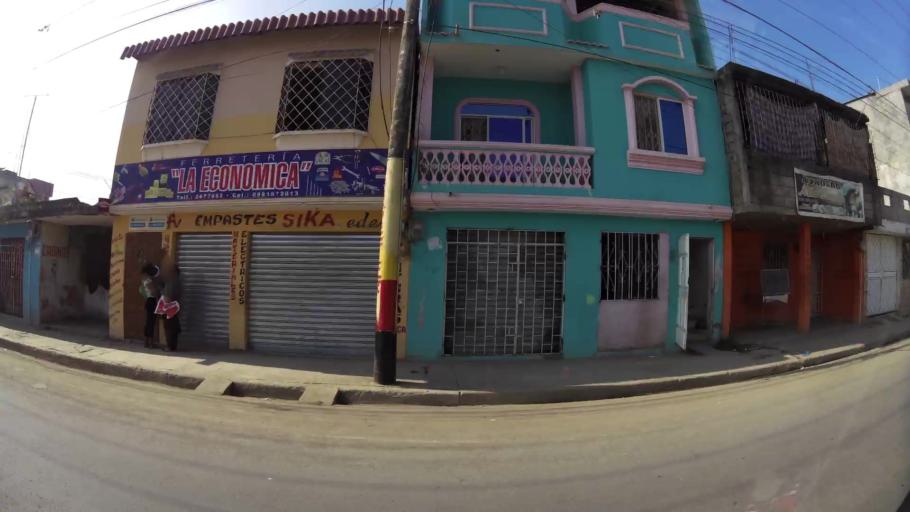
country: EC
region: Guayas
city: Eloy Alfaro
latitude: -2.1634
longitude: -79.7922
